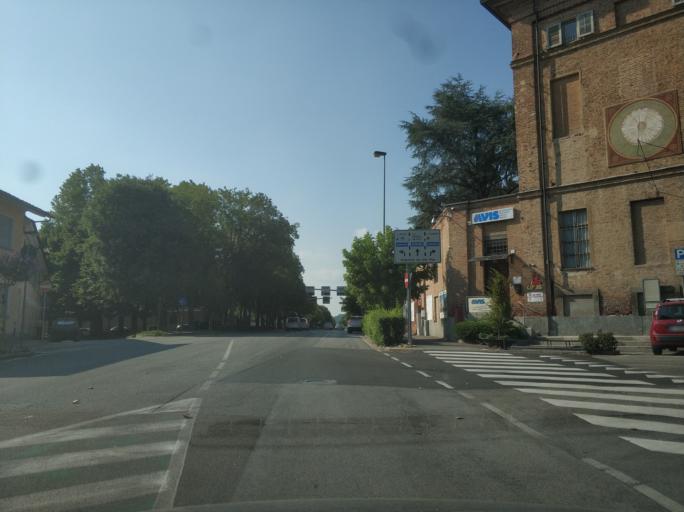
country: IT
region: Piedmont
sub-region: Provincia di Cuneo
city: Bra
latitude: 44.7018
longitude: 7.8476
